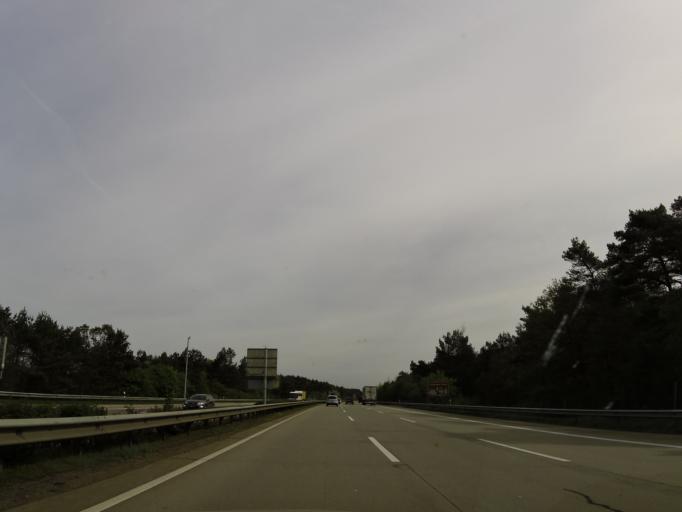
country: DE
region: Lower Saxony
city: Soltau
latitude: 53.0118
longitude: 9.9308
